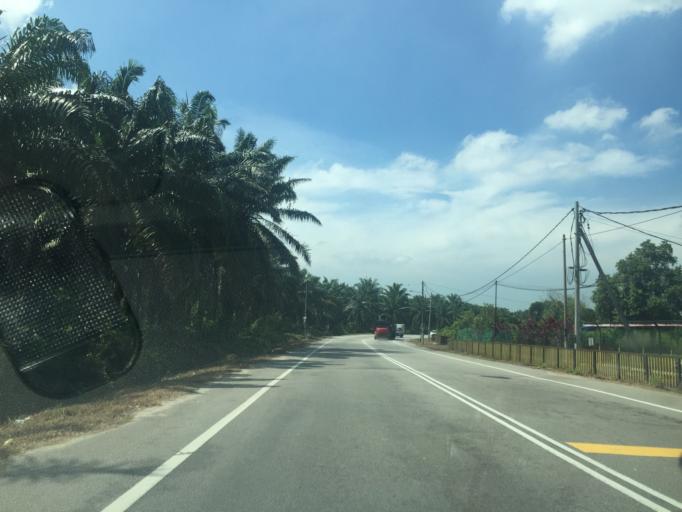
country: MY
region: Penang
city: Tasek Glugor
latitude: 5.4981
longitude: 100.5196
